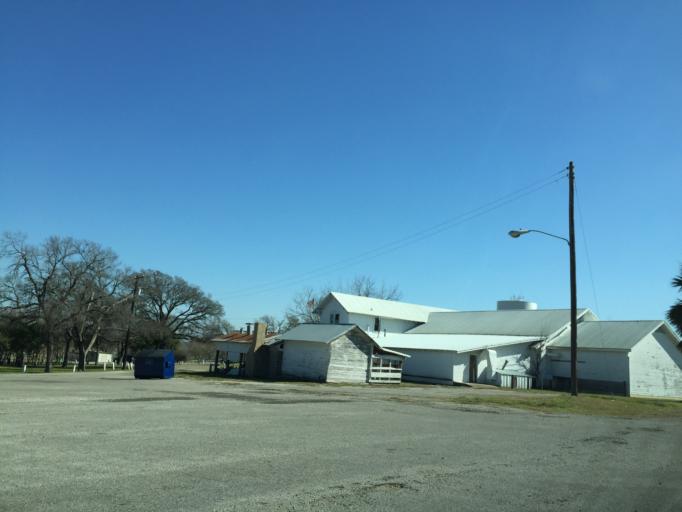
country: US
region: Texas
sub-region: Williamson County
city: Taylor
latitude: 30.5802
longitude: -97.4165
